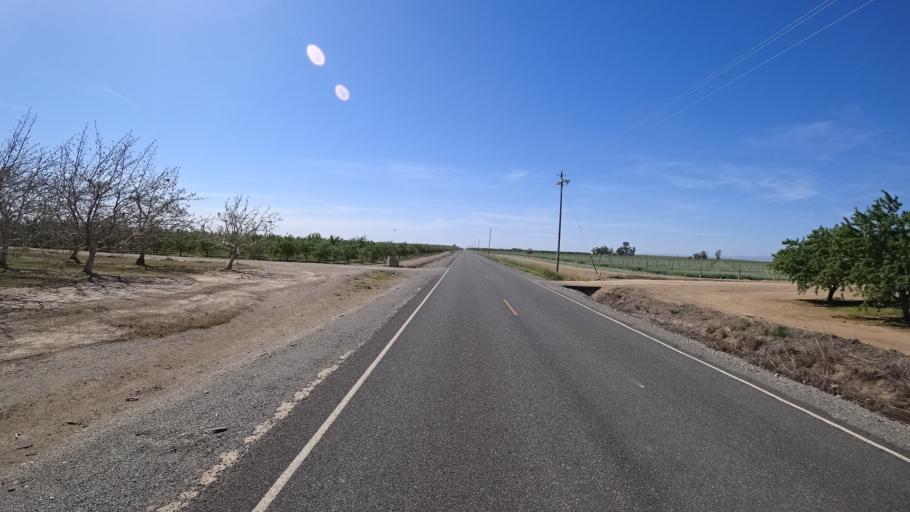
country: US
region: California
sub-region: Glenn County
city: Hamilton City
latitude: 39.6454
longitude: -122.1038
